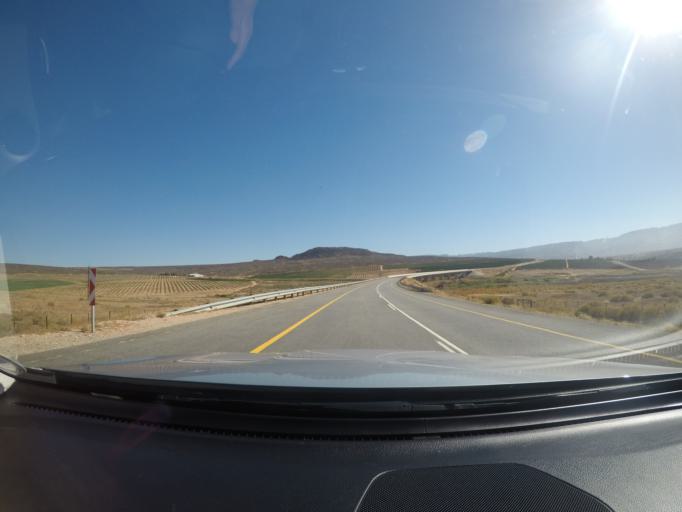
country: ZA
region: Western Cape
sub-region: West Coast District Municipality
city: Clanwilliam
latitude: -32.2059
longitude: 18.8611
